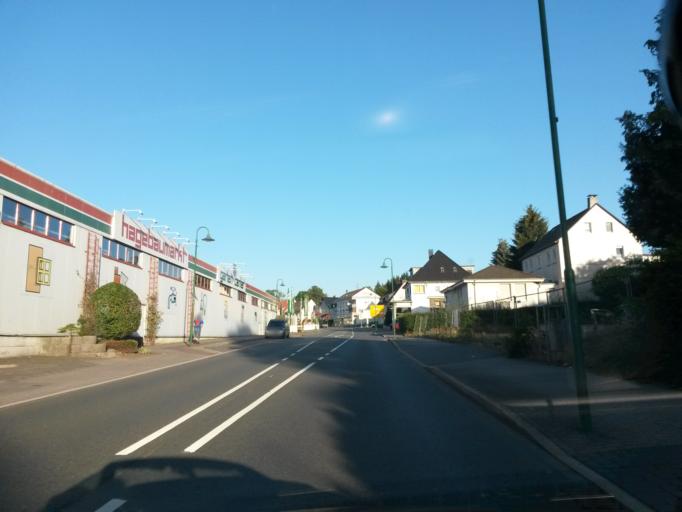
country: DE
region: North Rhine-Westphalia
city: Kierspe
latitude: 51.1248
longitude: 7.6074
